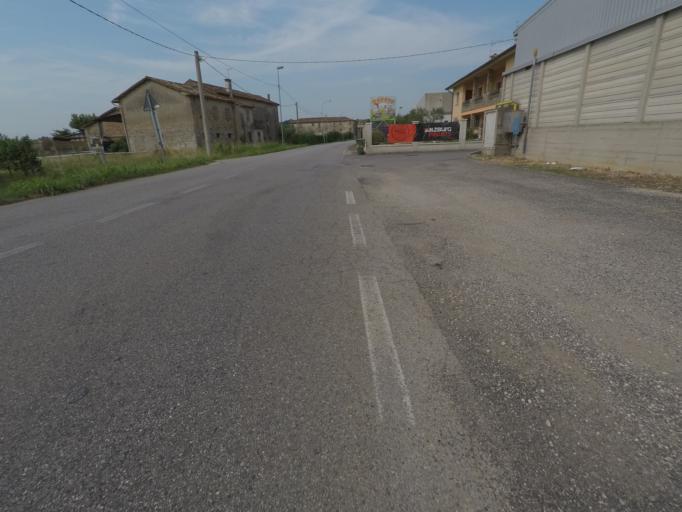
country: IT
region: Veneto
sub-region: Provincia di Treviso
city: Carpesica
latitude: 45.9575
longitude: 12.3071
